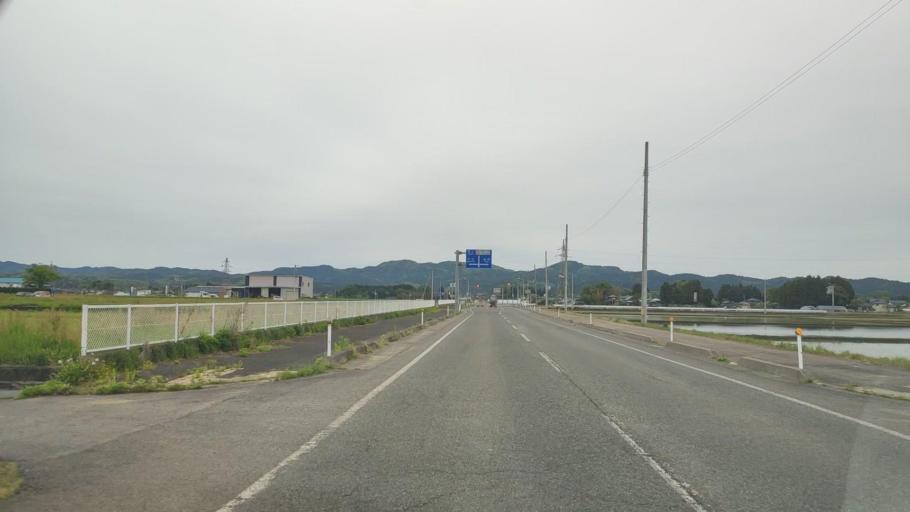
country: JP
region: Niigata
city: Gosen
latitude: 37.7293
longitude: 139.1684
